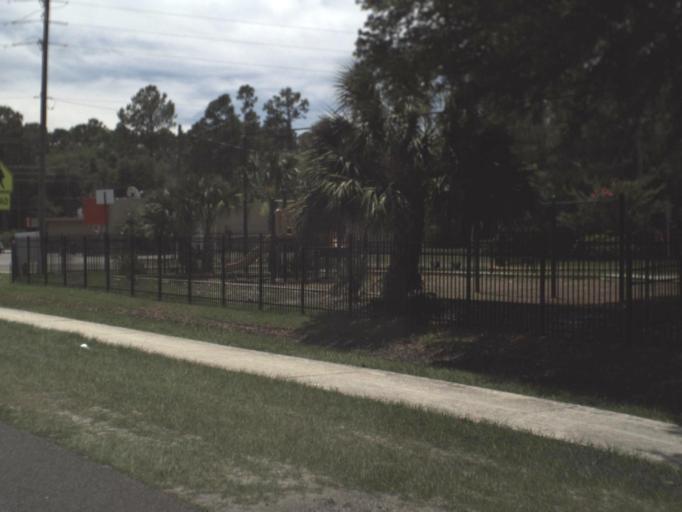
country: US
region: Florida
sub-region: Duval County
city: Jacksonville
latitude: 30.3957
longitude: -81.7384
